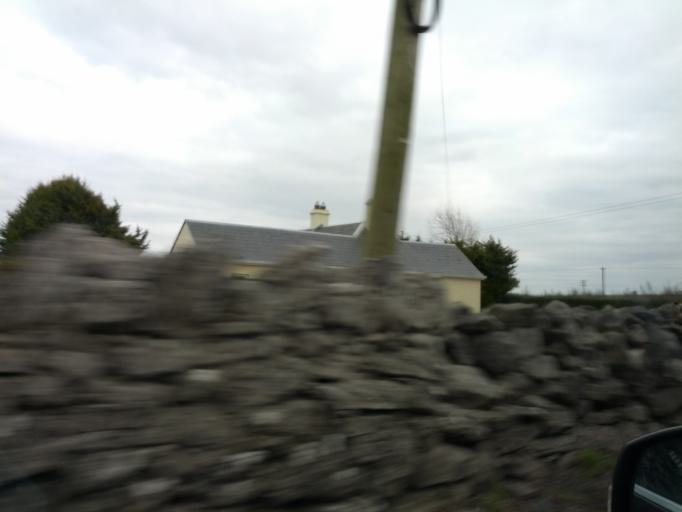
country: IE
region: Connaught
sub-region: County Galway
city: Athenry
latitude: 53.2833
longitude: -8.7438
